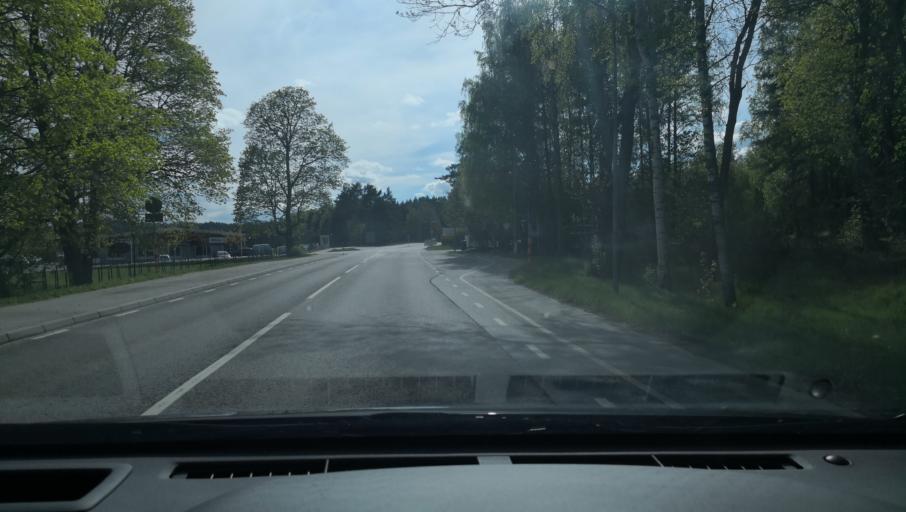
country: SE
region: OErebro
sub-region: Askersunds Kommun
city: Asbro
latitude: 59.0548
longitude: 15.0540
